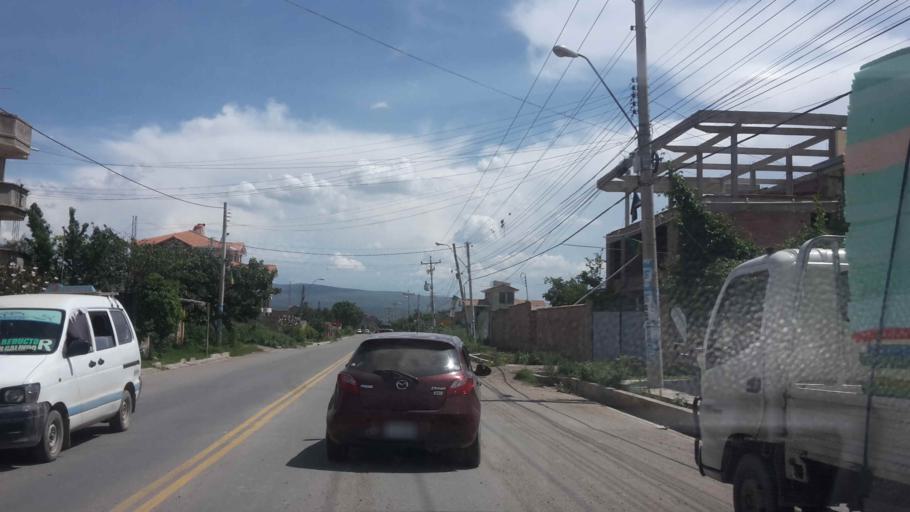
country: BO
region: Cochabamba
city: Cochabamba
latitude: -17.3655
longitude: -66.2304
